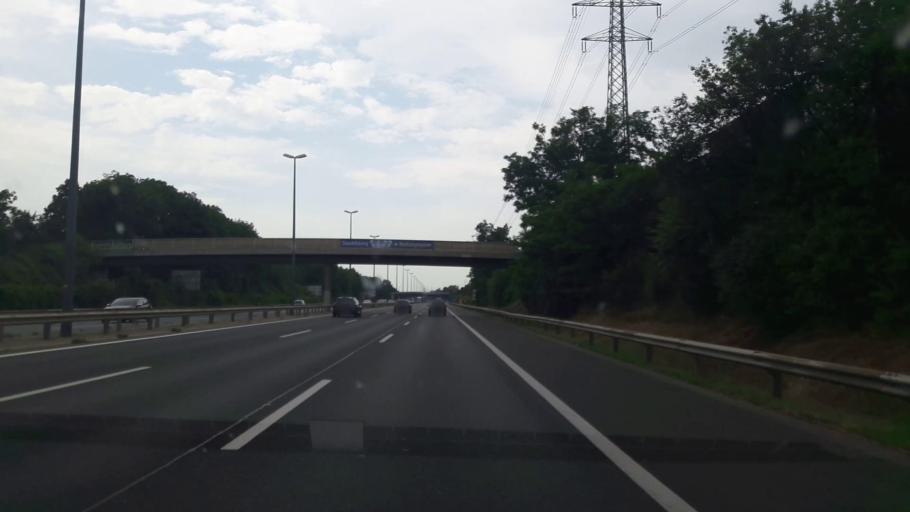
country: AT
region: Lower Austria
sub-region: Politischer Bezirk Korneuburg
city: Langenzersdorf
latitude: 48.2742
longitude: 16.3712
